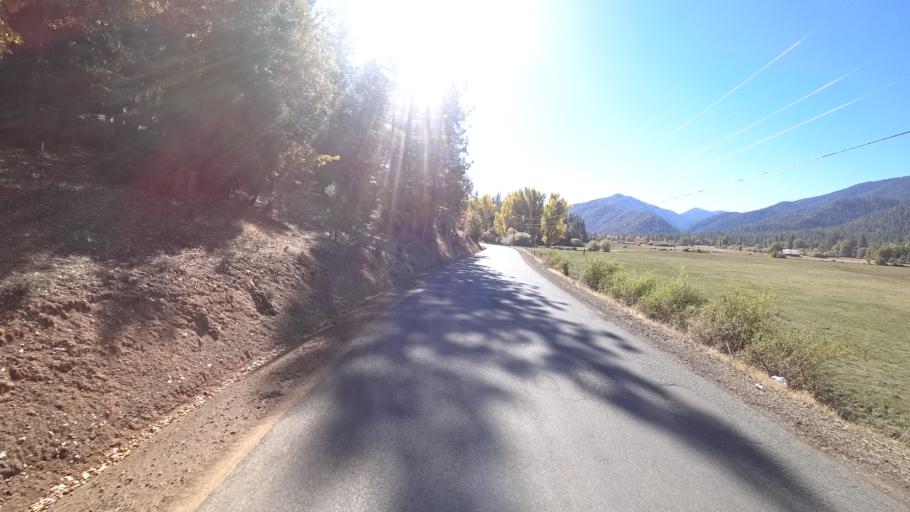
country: US
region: California
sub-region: Siskiyou County
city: Yreka
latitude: 41.6093
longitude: -122.9793
